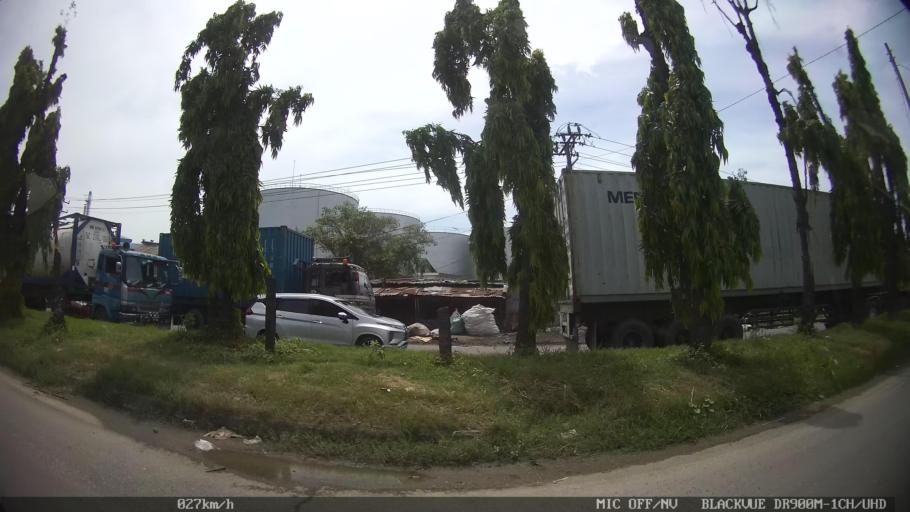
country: ID
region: North Sumatra
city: Belawan
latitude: 3.7792
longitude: 98.6875
